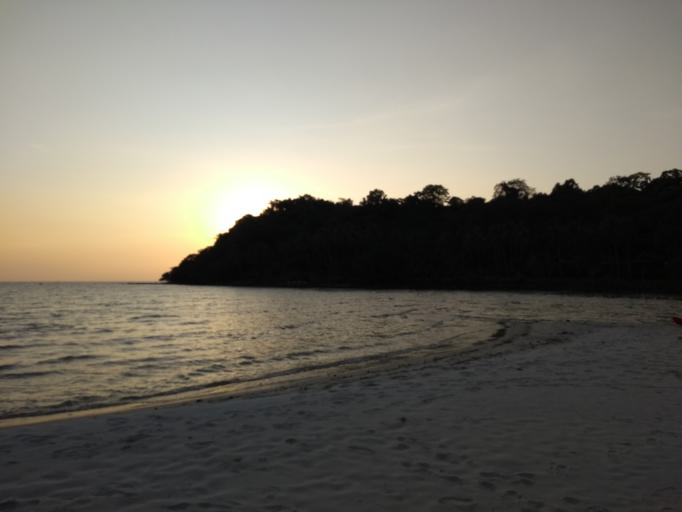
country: TH
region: Trat
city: Ko Kut
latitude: 11.6373
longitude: 102.5440
